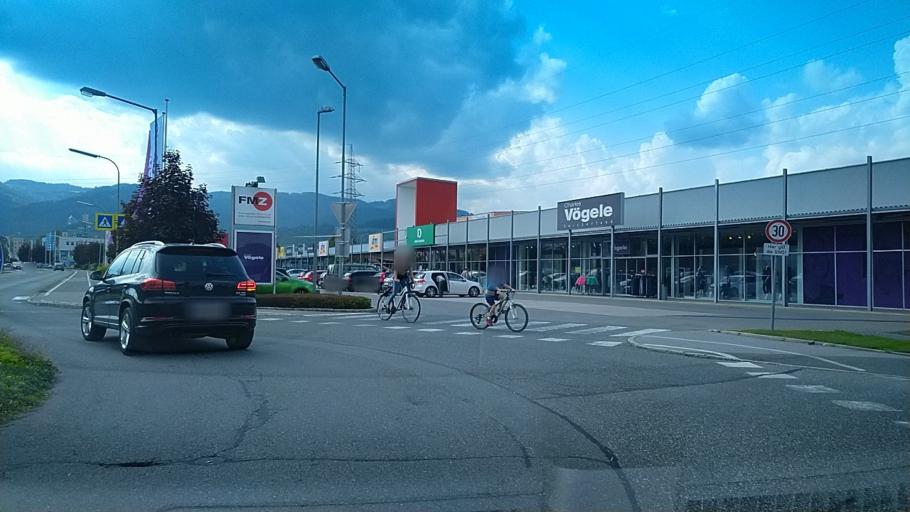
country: AT
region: Styria
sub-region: Politischer Bezirk Deutschlandsberg
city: Deutschlandsberg
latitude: 46.8204
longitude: 15.2307
